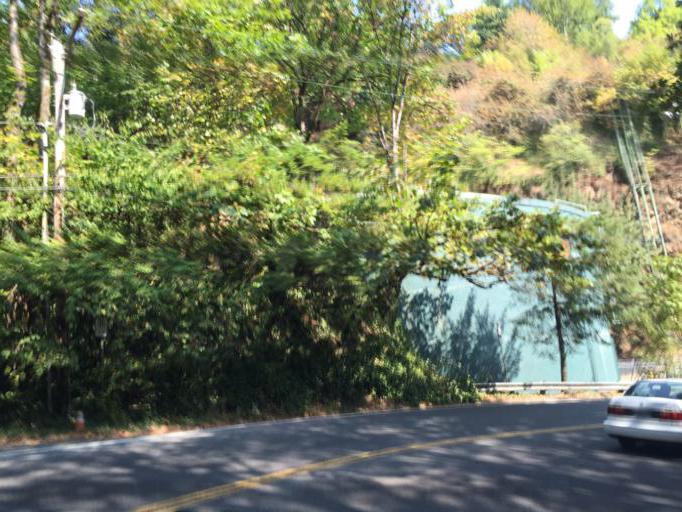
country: US
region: Oregon
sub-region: Multnomah County
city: Portland
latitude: 45.5026
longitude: -122.6910
